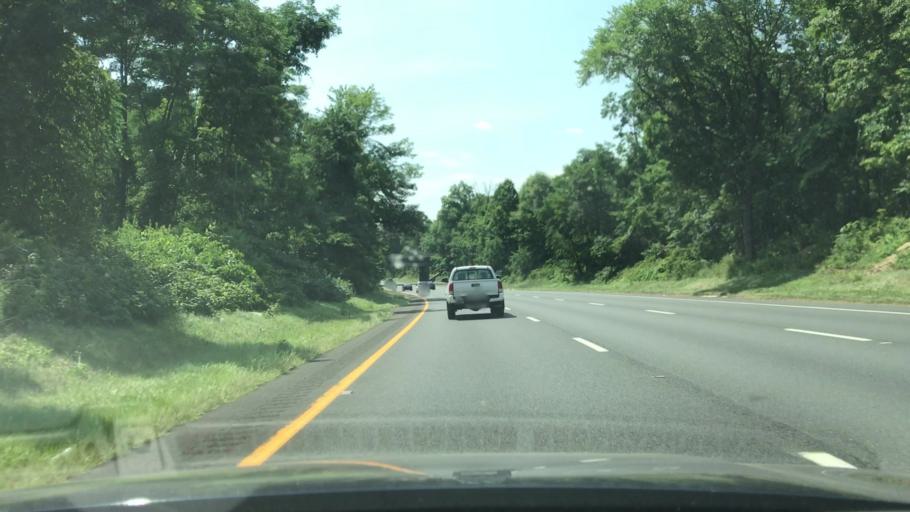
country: US
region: New Jersey
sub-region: Somerset County
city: Finderne
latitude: 40.5802
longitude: -74.5771
